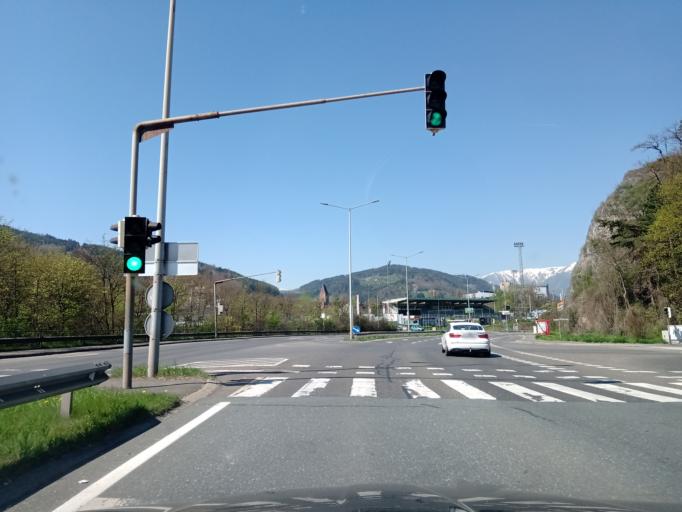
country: AT
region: Styria
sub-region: Politischer Bezirk Leoben
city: Leoben
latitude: 47.3761
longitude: 15.0824
